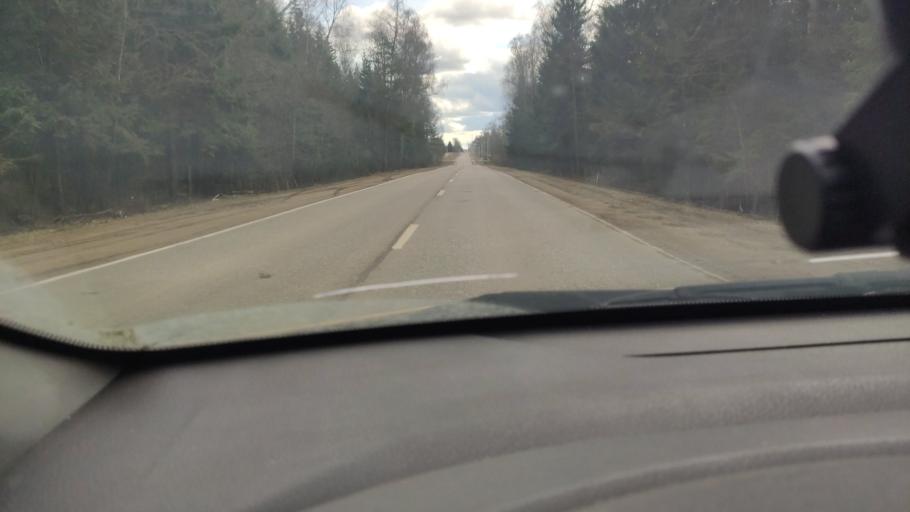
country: RU
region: Moskovskaya
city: Ruza
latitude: 55.7198
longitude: 36.1645
